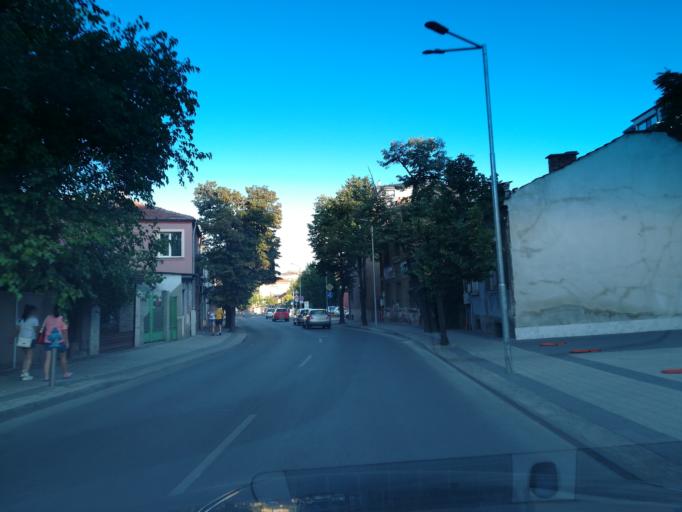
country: BG
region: Plovdiv
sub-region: Obshtina Plovdiv
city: Plovdiv
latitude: 42.1414
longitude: 24.7353
